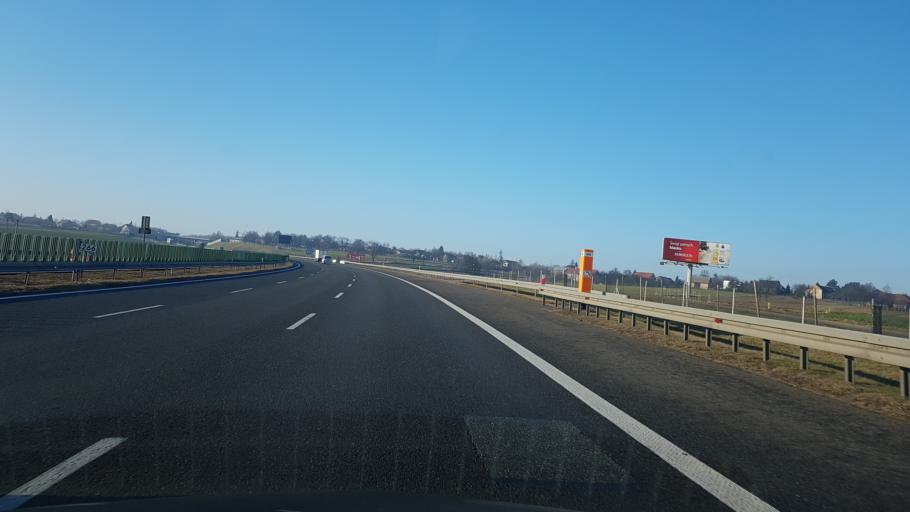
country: PL
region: Opole Voivodeship
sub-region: Powiat strzelecki
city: Lesnica
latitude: 50.4668
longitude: 18.1751
